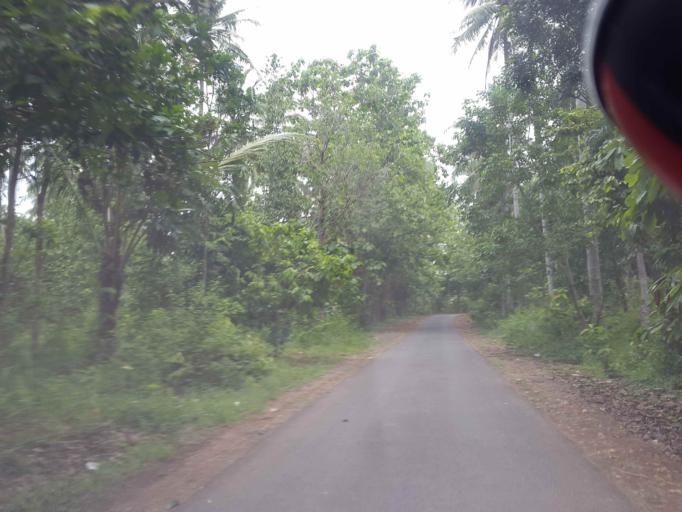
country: ID
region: Lampung
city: Natar
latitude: -5.3154
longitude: 105.2461
